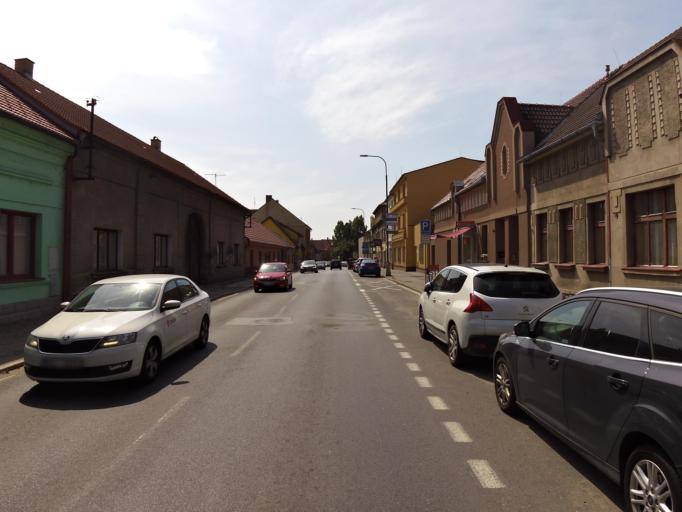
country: CZ
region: Central Bohemia
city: Lysa nad Labem
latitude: 50.2039
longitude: 14.8431
